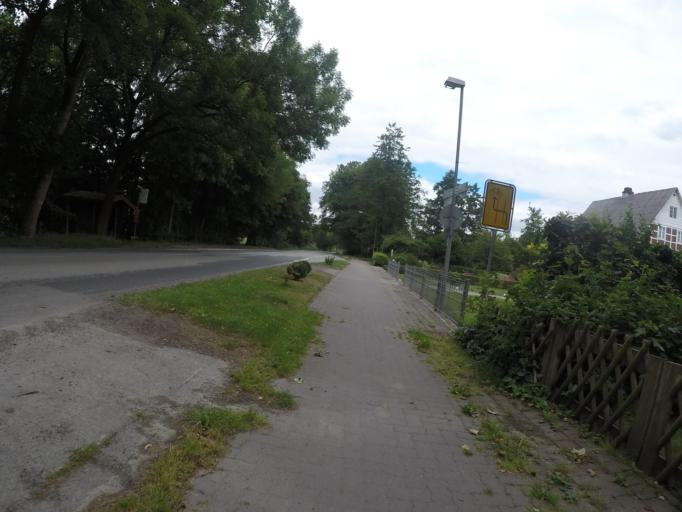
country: DE
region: Lower Saxony
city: Grossenworden
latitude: 53.6595
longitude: 9.2942
